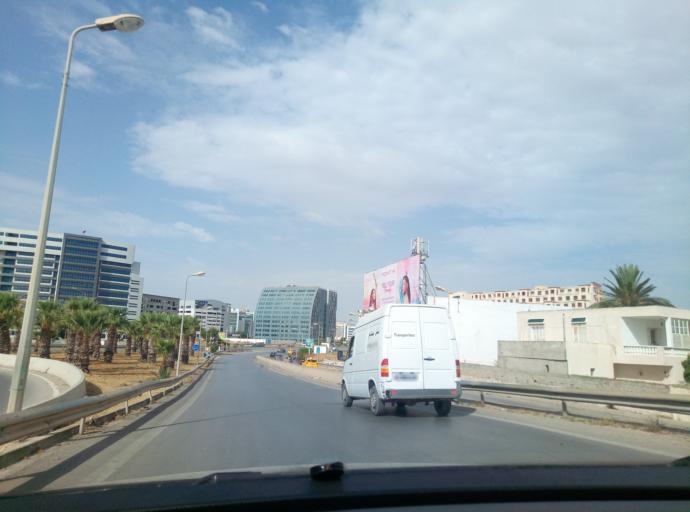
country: TN
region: Ariana
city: Ariana
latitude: 36.8514
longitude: 10.2015
